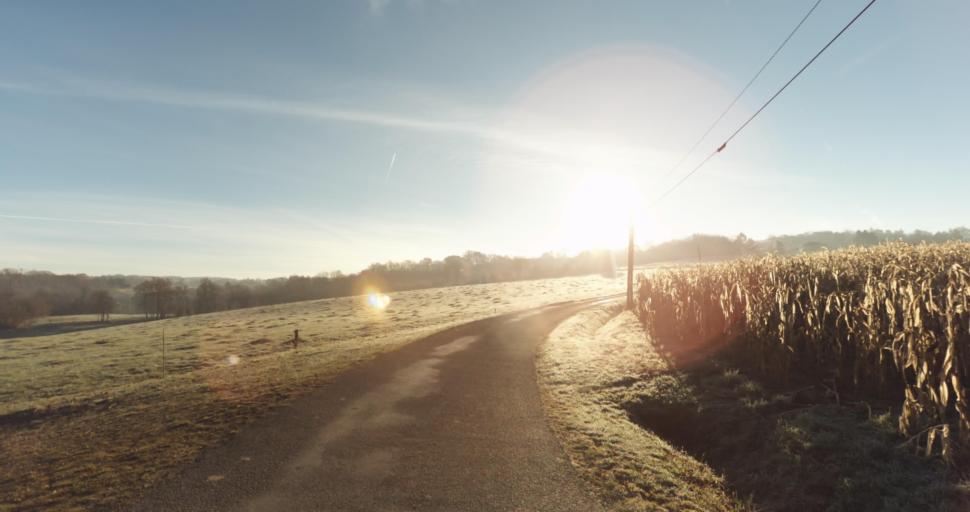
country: FR
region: Limousin
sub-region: Departement de la Haute-Vienne
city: Aixe-sur-Vienne
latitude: 45.8233
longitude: 1.1466
